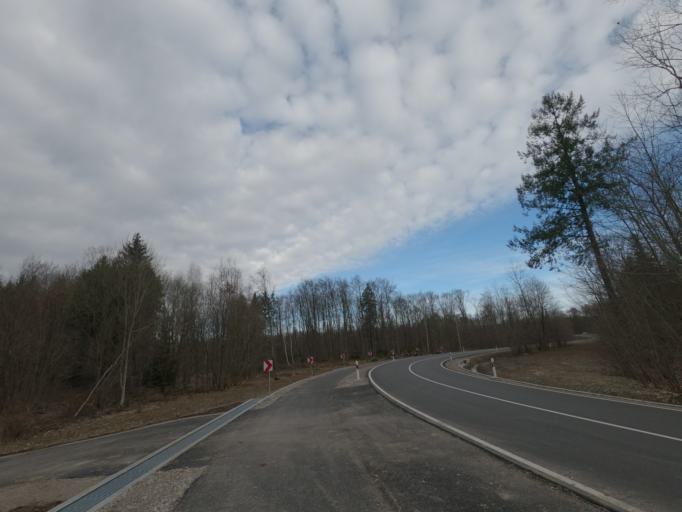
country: DE
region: Baden-Wuerttemberg
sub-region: Regierungsbezirk Stuttgart
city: Ohmden
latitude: 48.6548
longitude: 9.5275
